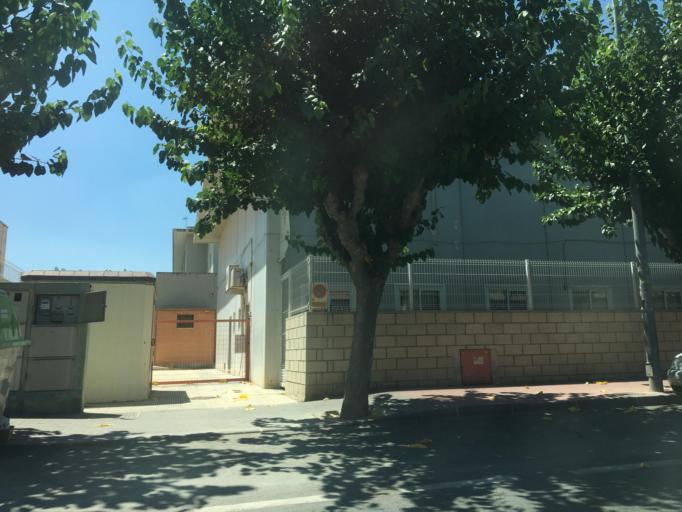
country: ES
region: Murcia
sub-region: Murcia
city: Murcia
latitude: 38.0063
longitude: -1.1163
